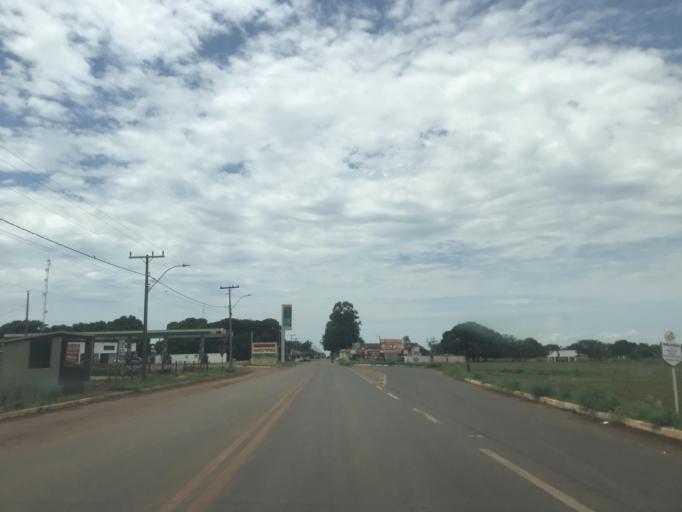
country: BR
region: Goias
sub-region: Luziania
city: Luziania
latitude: -16.3106
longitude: -48.0141
